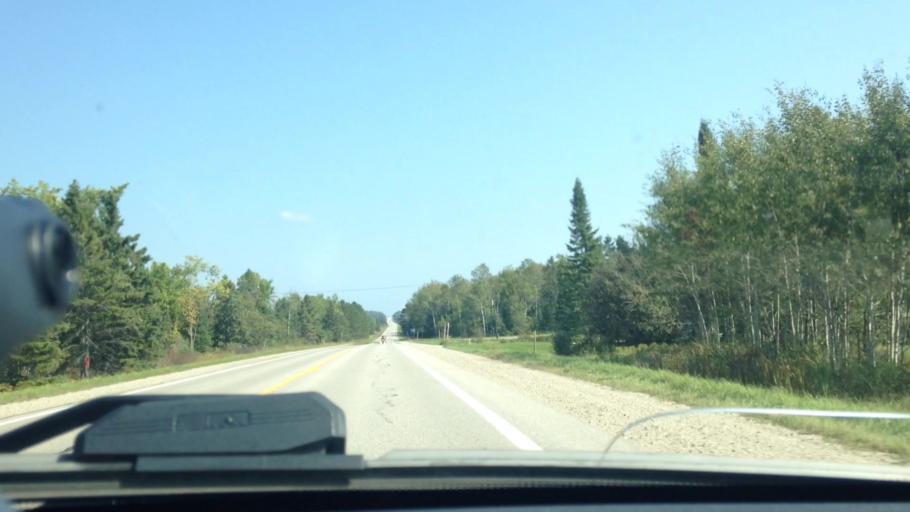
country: US
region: Michigan
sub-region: Luce County
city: Newberry
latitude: 46.3105
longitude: -85.5964
